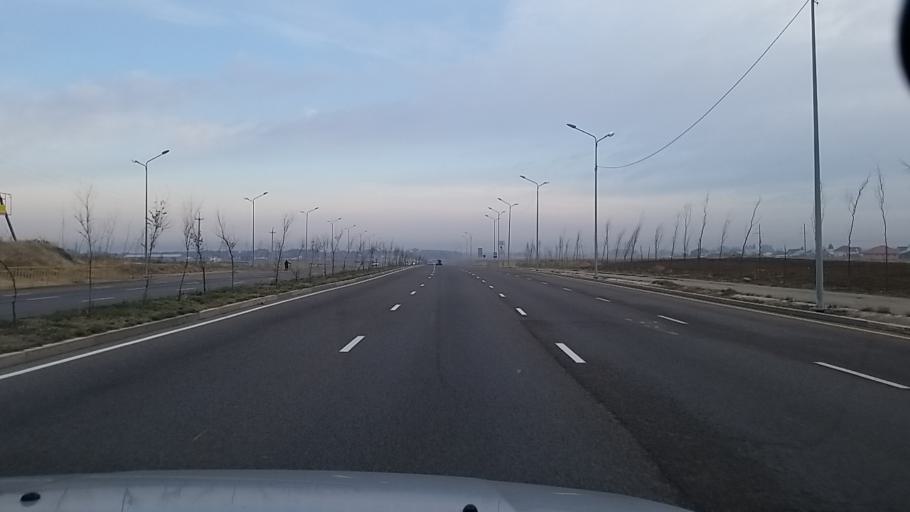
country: KZ
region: Almaty Oblysy
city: Burunday
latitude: 43.3404
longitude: 76.8337
